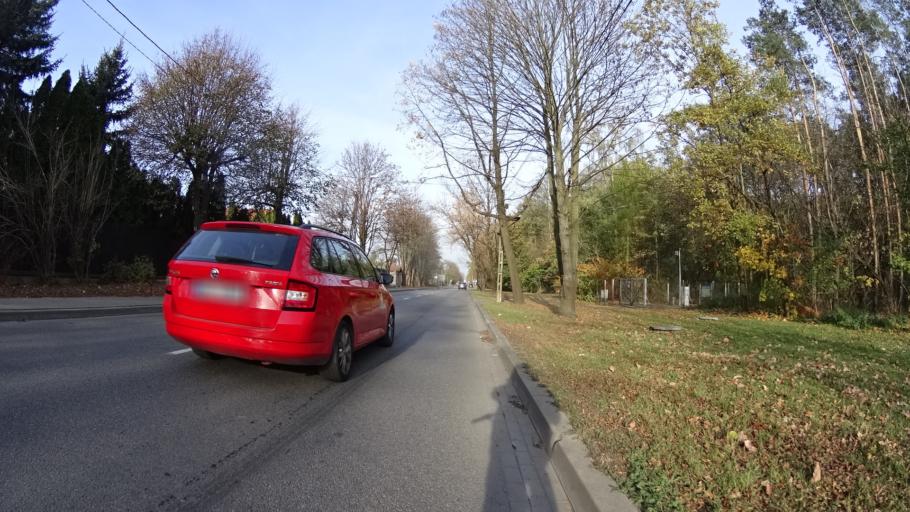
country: PL
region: Masovian Voivodeship
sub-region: Powiat warszawski zachodni
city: Babice
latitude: 52.2630
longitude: 20.8555
